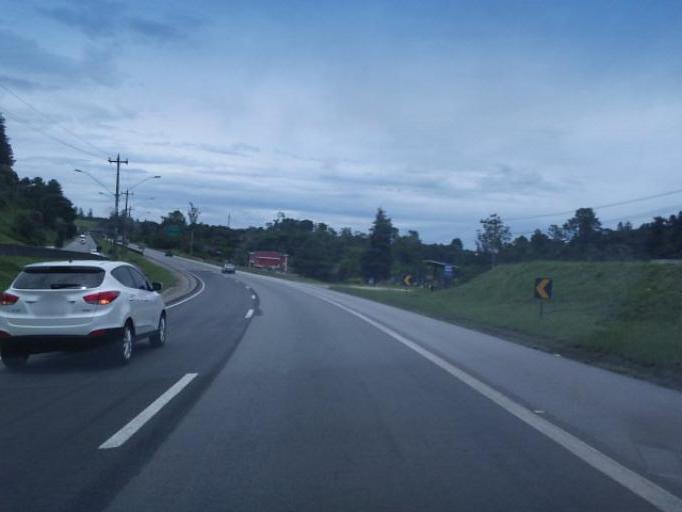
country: BR
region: Sao Paulo
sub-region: Sao Lourenco Da Serra
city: Sao Lourenco da Serra
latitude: -23.8454
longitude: -46.9372
